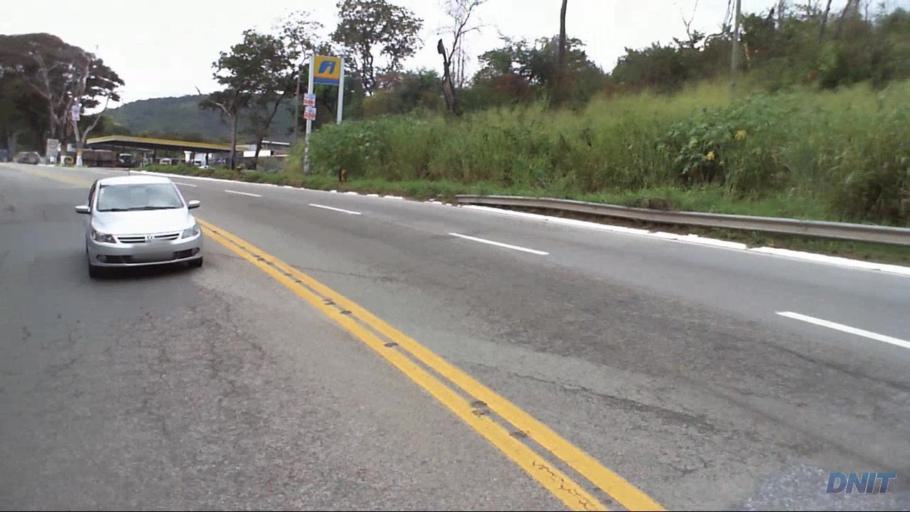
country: BR
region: Minas Gerais
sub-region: Caete
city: Caete
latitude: -19.7884
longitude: -43.7315
